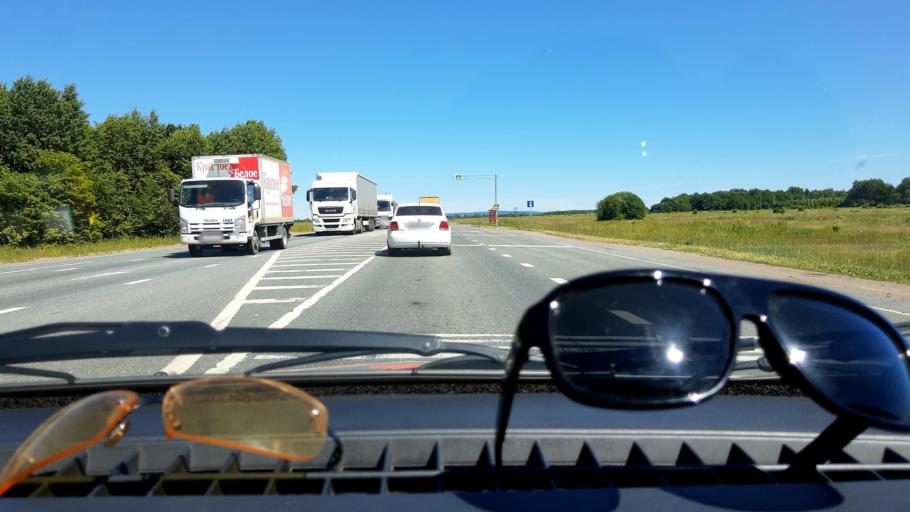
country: RU
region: Bashkortostan
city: Kudeyevskiy
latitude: 54.8171
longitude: 56.7947
